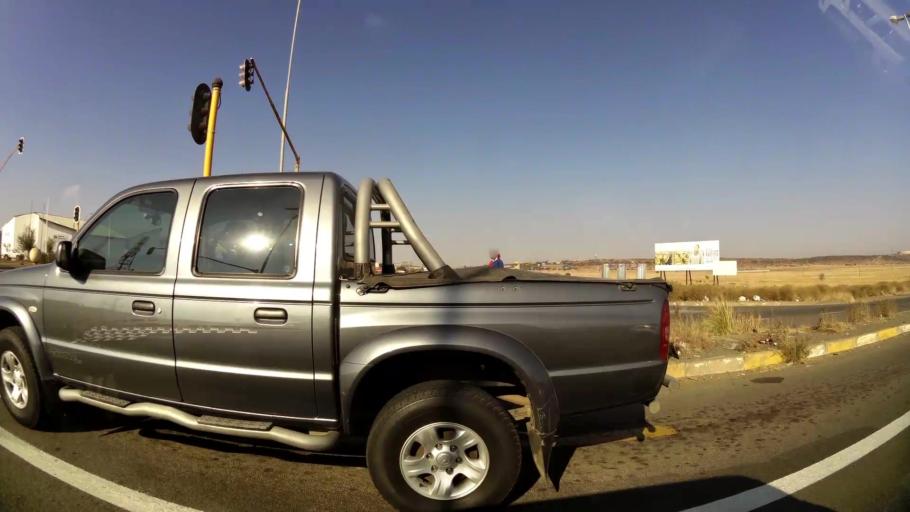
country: ZA
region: Orange Free State
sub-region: Mangaung Metropolitan Municipality
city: Bloemfontein
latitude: -29.1728
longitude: 26.2200
